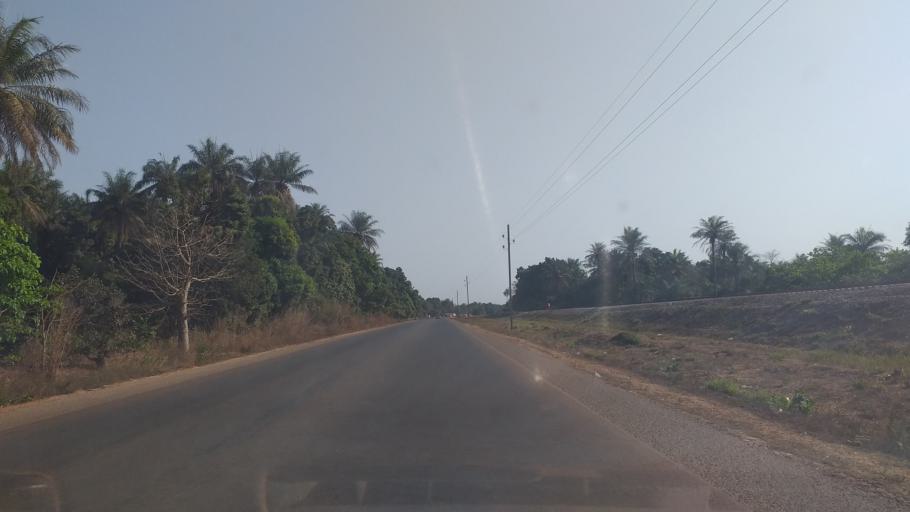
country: GN
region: Boke
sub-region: Boke Prefecture
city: Kamsar
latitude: 10.7323
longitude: -14.5169
